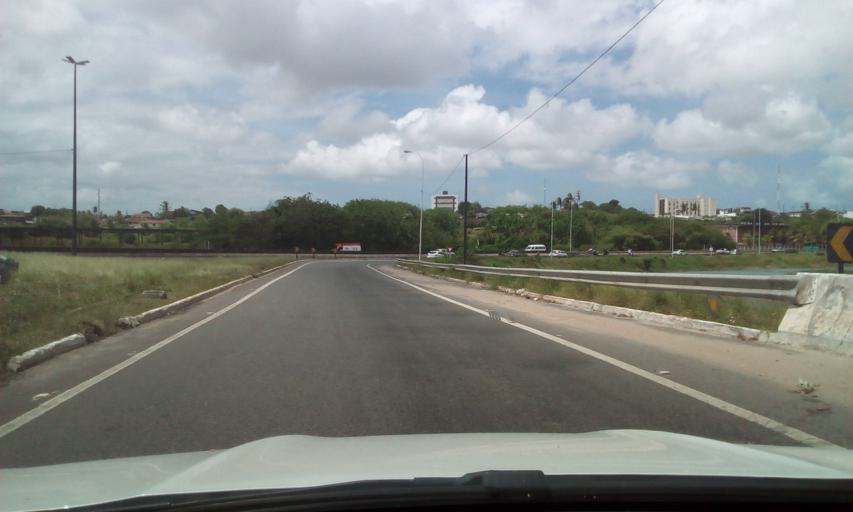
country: BR
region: Paraiba
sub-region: Bayeux
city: Bayeux
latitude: -7.1661
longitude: -34.8947
